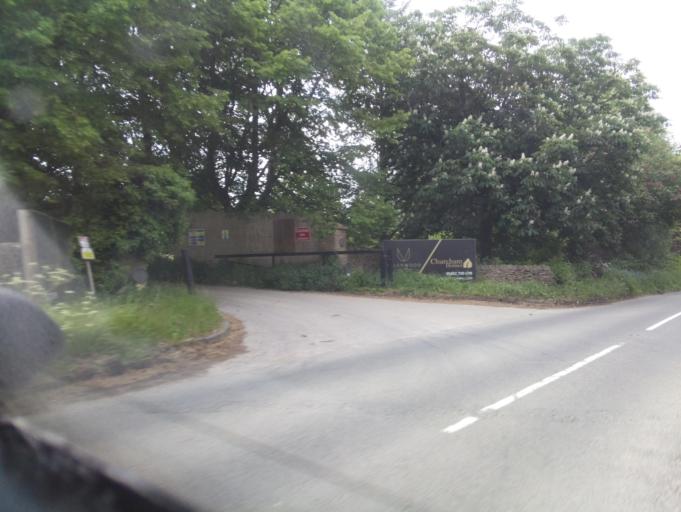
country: GB
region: England
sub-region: Gloucestershire
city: Shurdington
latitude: 51.8516
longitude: -2.0857
